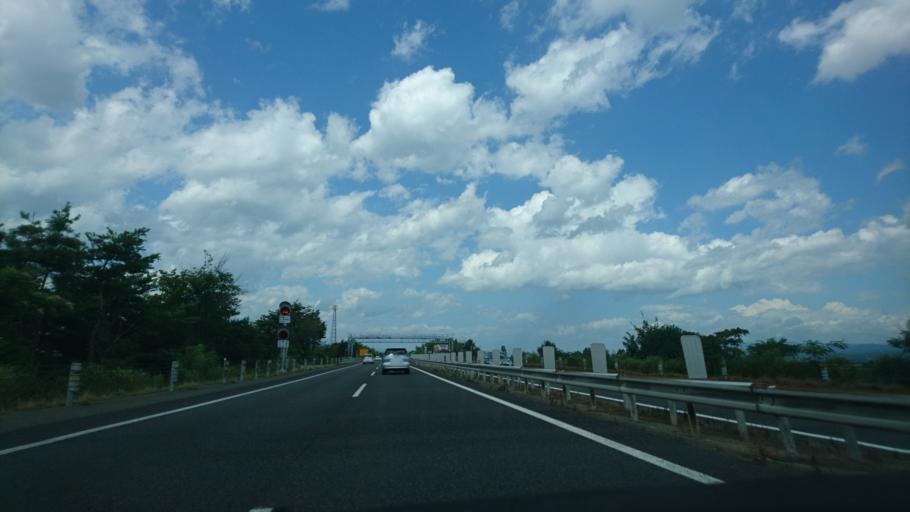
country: JP
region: Iwate
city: Morioka-shi
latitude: 39.6241
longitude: 141.1290
